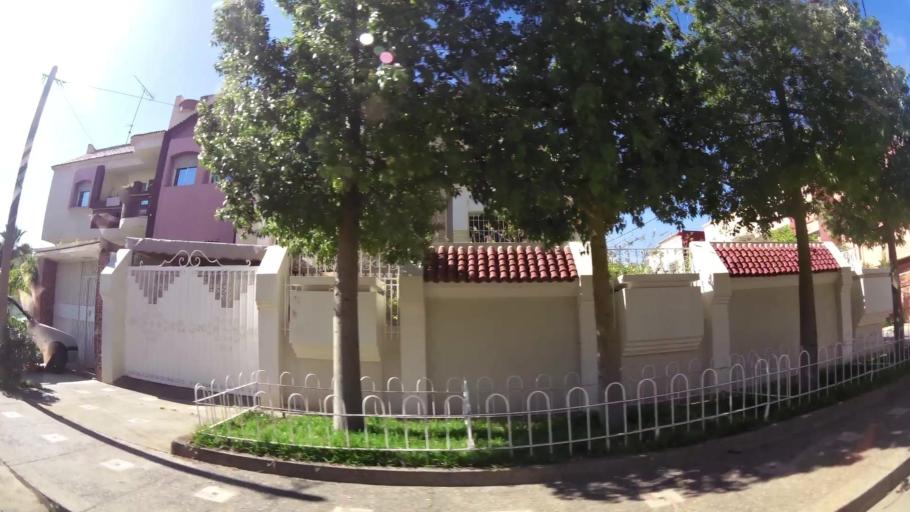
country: MA
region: Oriental
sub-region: Oujda-Angad
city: Oujda
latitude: 34.6635
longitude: -1.8975
